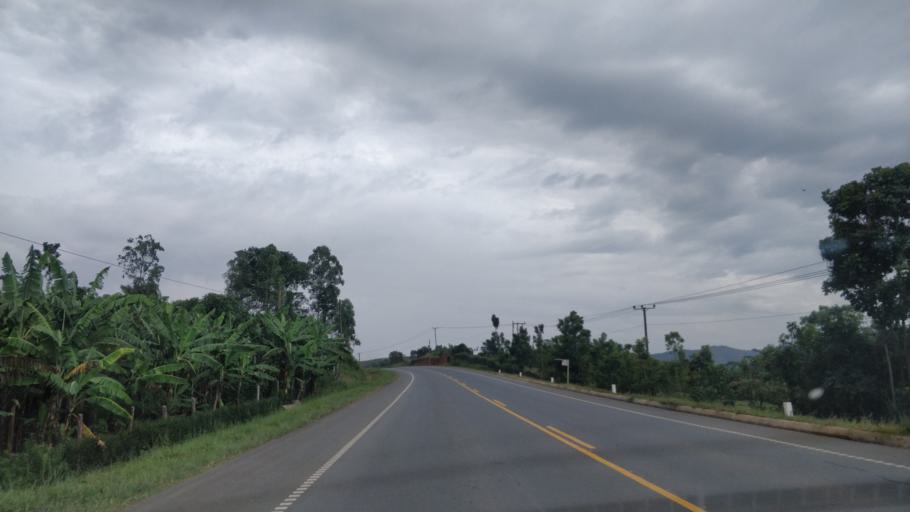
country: UG
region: Western Region
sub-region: Sheema District
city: Kibingo
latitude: -0.6558
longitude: 30.4794
